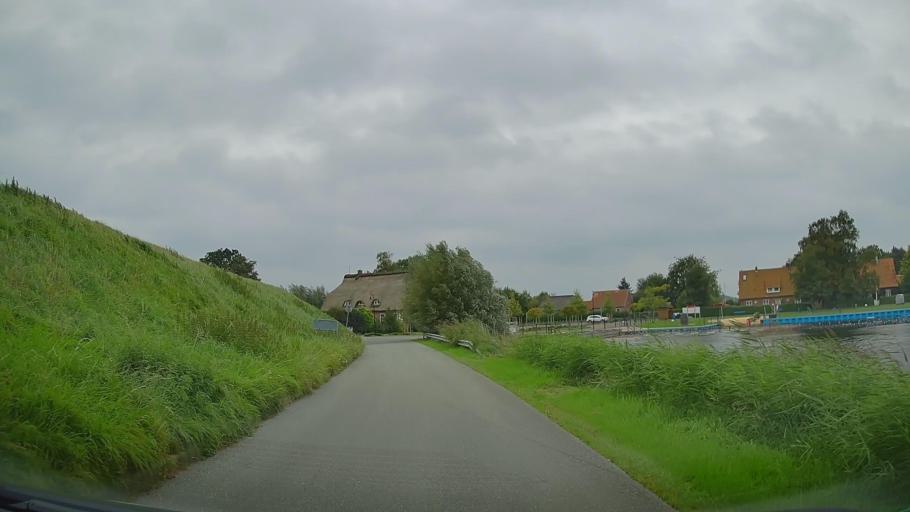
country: DE
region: Lower Saxony
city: Krummendeich
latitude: 53.8323
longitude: 9.2021
